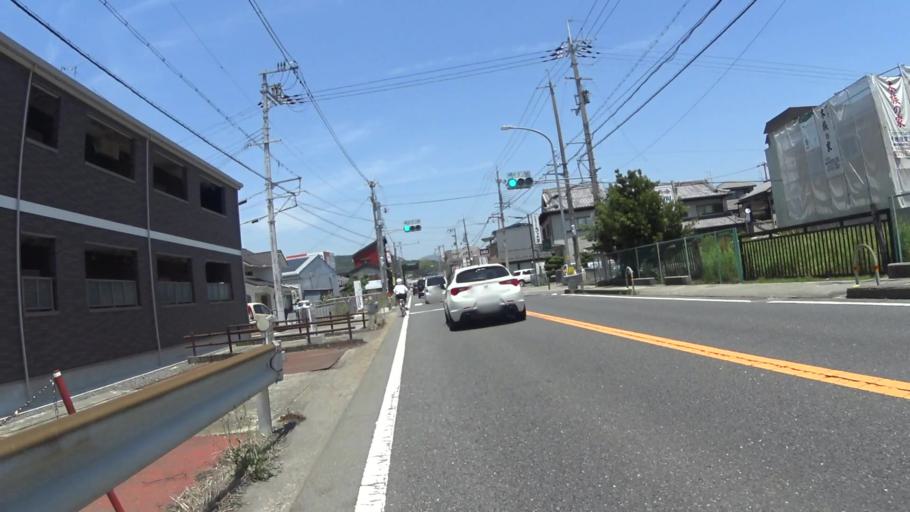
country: JP
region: Kyoto
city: Kameoka
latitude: 35.0462
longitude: 135.5456
